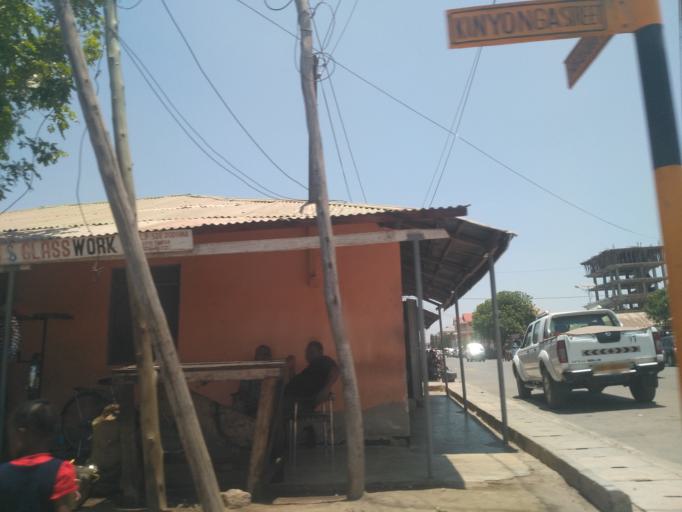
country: TZ
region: Dodoma
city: Dodoma
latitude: -6.1751
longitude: 35.7430
